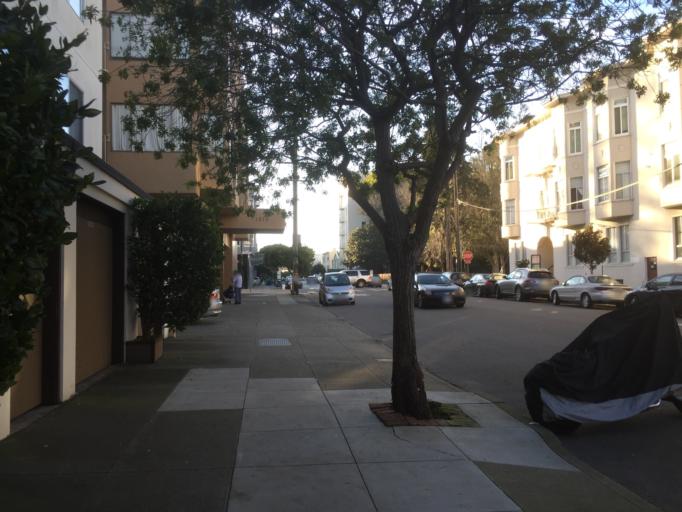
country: US
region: California
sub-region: San Francisco County
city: San Francisco
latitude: 37.7973
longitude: -122.4264
